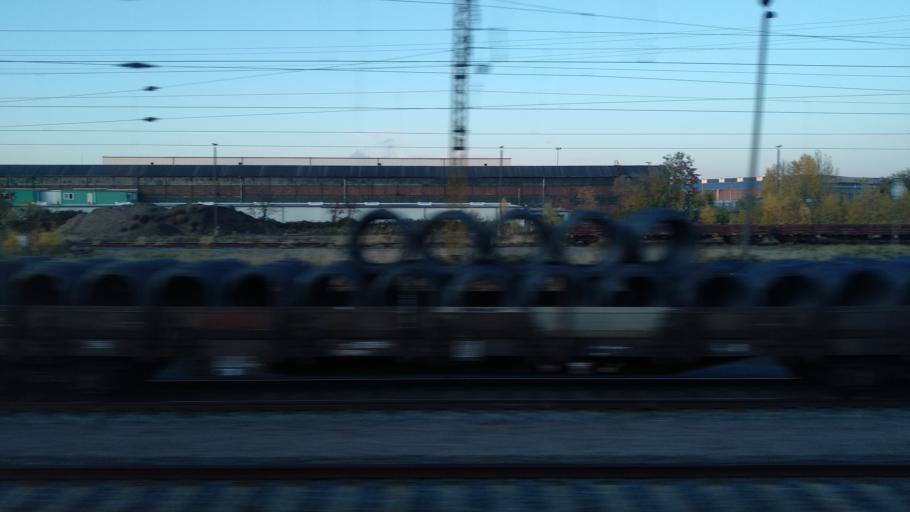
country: DE
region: Saxony
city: Riesa
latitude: 51.3093
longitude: 13.2825
